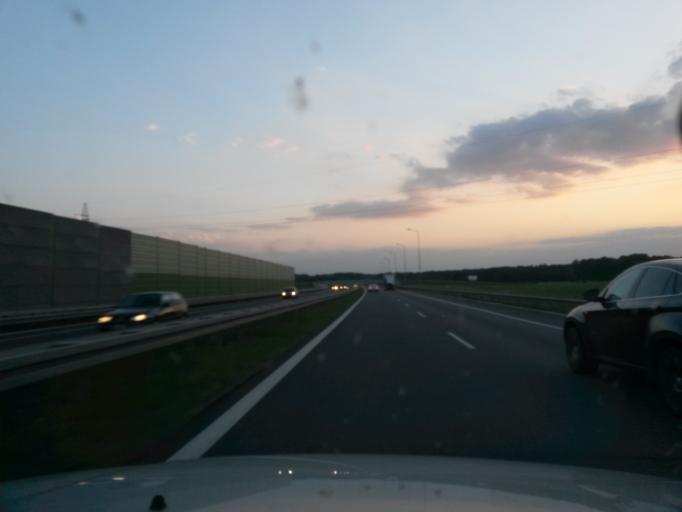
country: PL
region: Lower Silesian Voivodeship
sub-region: Powiat olesnicki
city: Sycow
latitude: 51.2983
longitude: 17.7514
